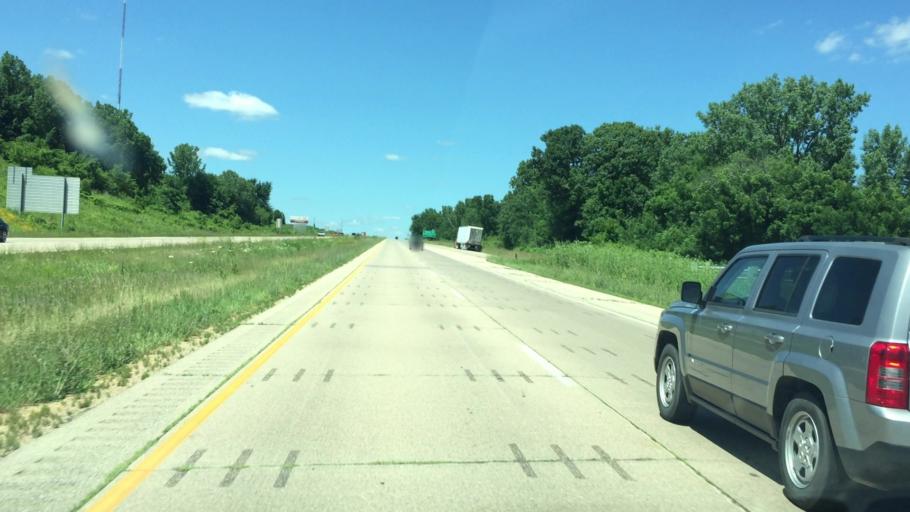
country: US
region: Illinois
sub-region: Jo Daviess County
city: East Dubuque
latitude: 42.5215
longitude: -90.6145
